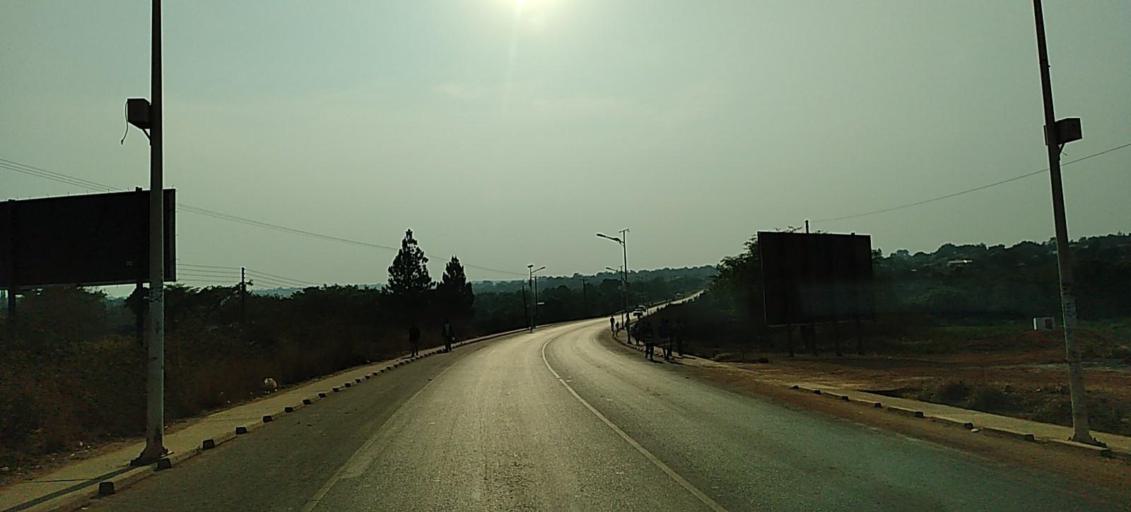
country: ZM
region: North-Western
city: Solwezi
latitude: -12.1884
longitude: 26.4298
